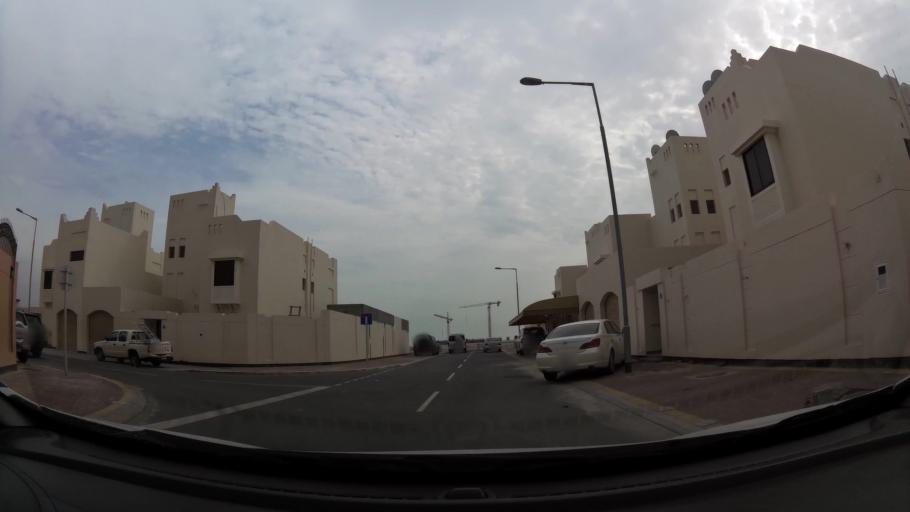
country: BH
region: Northern
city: Ar Rifa'
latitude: 26.0513
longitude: 50.6189
